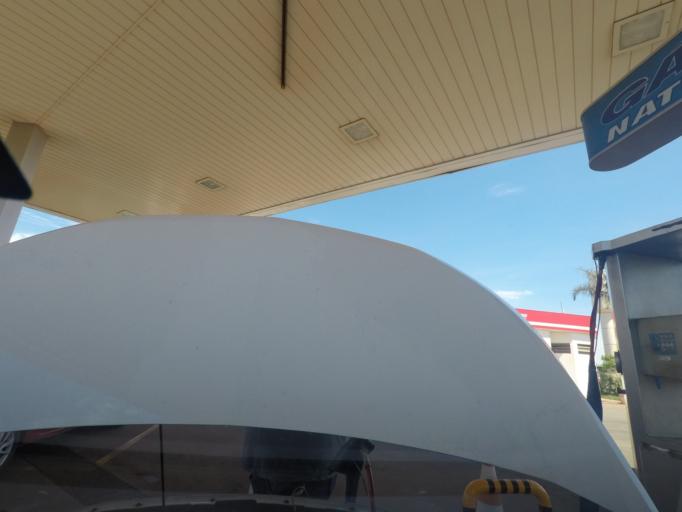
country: BR
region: Sao Paulo
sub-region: Araraquara
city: Araraquara
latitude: -21.8201
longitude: -48.1742
